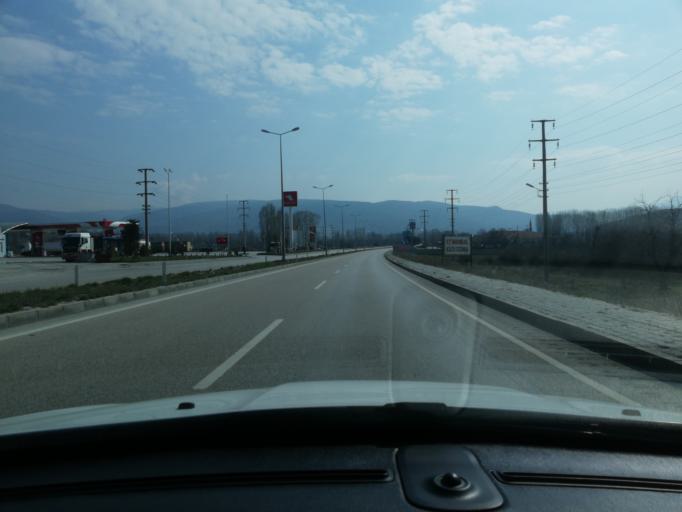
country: TR
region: Cankiri
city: Ilgaz
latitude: 40.9084
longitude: 33.6283
